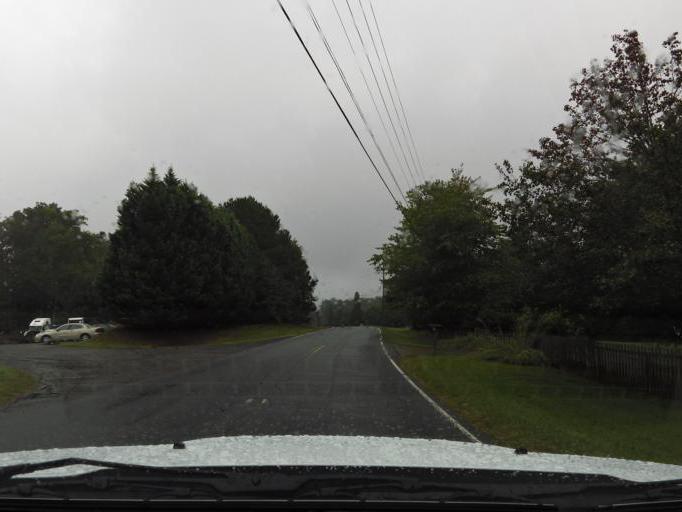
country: US
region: Georgia
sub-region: Cobb County
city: Acworth
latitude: 34.0564
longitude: -84.6462
